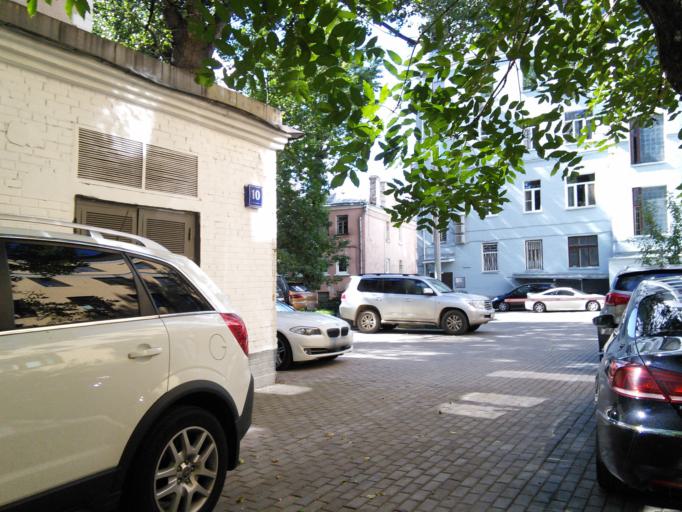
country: RU
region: Moscow
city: Moscow
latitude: 55.7588
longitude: 37.6360
